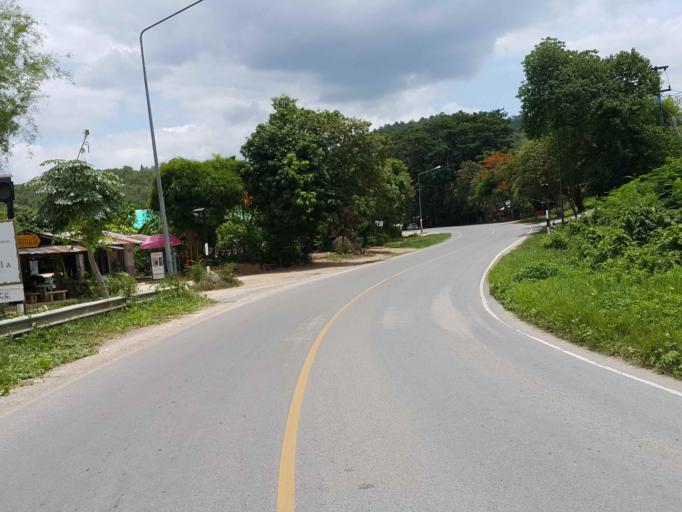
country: TH
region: Chiang Mai
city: Hang Dong
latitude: 18.7525
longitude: 98.8884
